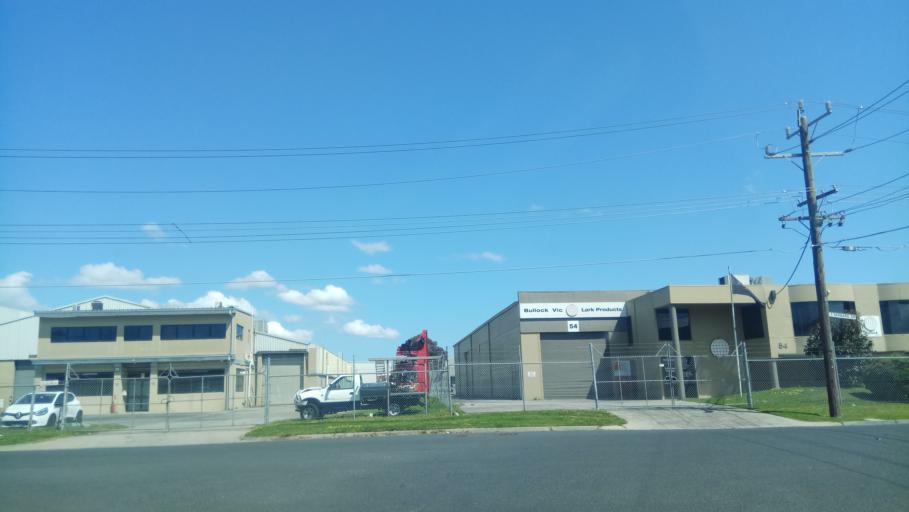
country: AU
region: Victoria
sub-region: Kingston
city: Dingley Village
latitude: -37.9895
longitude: 145.1154
